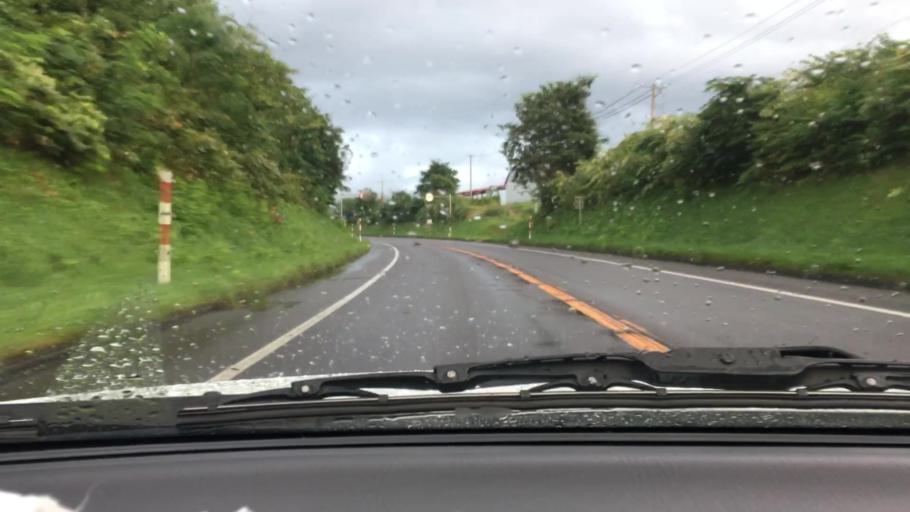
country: JP
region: Hokkaido
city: Nanae
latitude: 42.0819
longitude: 140.5879
